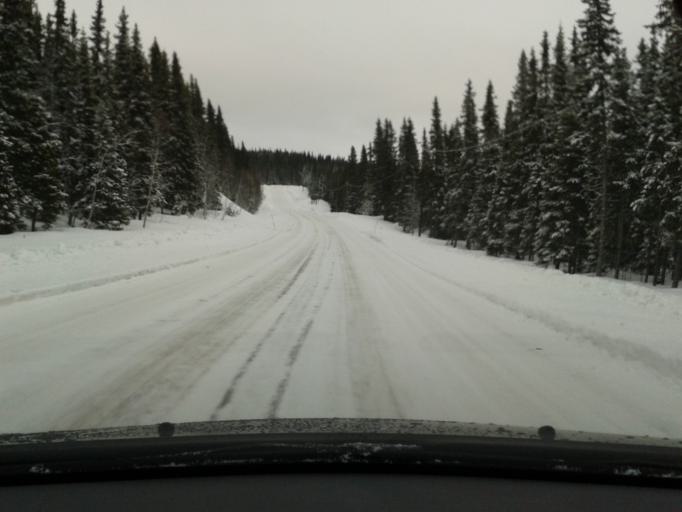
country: SE
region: Vaesterbotten
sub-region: Vilhelmina Kommun
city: Sjoberg
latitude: 65.2292
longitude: 15.9729
